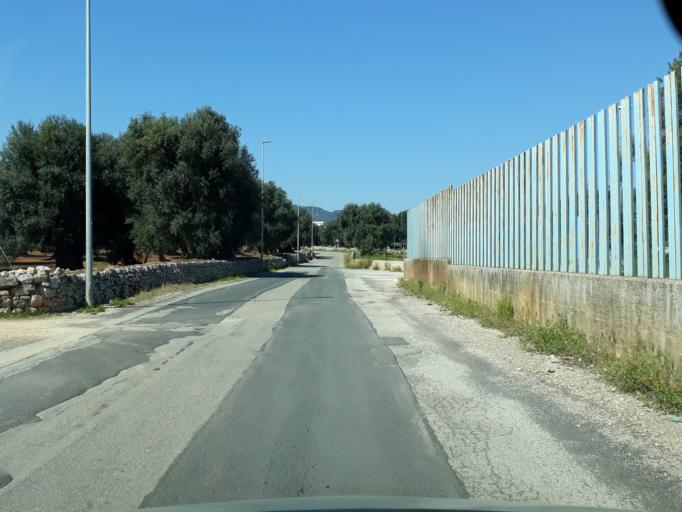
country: IT
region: Apulia
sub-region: Provincia di Brindisi
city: Fasano
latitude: 40.8356
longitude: 17.3701
